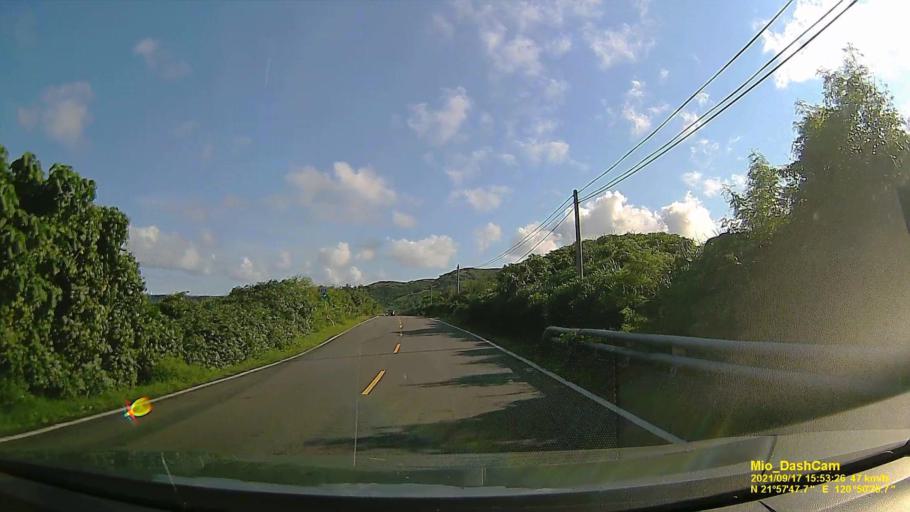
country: TW
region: Taiwan
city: Hengchun
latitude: 21.9632
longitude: 120.8405
